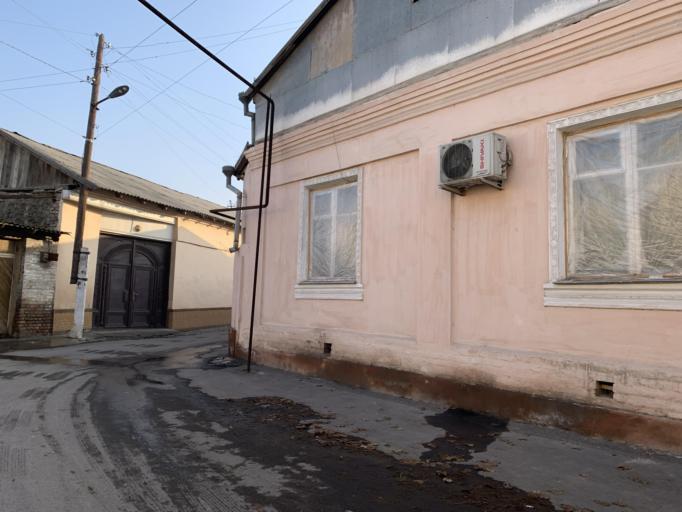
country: UZ
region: Fergana
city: Qo`qon
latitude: 40.5423
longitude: 70.9320
